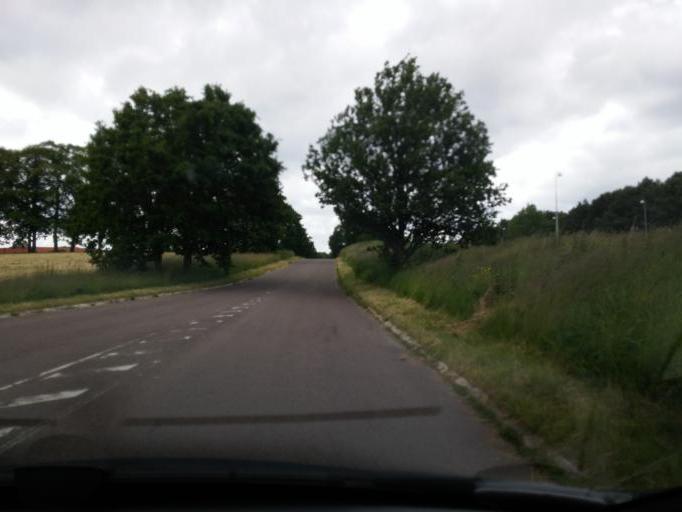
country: DK
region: Capital Region
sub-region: Hillerod Kommune
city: Hillerod
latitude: 55.9207
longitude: 12.2884
